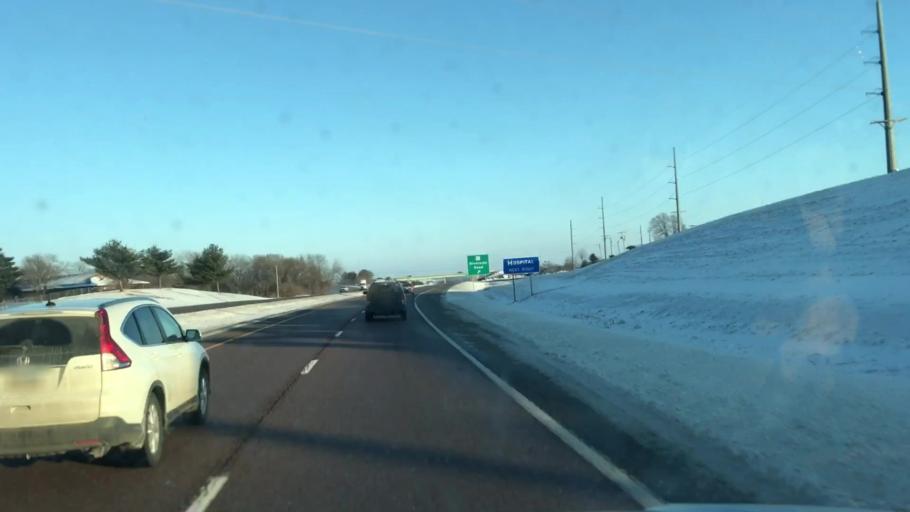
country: US
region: Missouri
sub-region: Buchanan County
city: Saint Joseph
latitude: 39.7512
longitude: -94.7754
